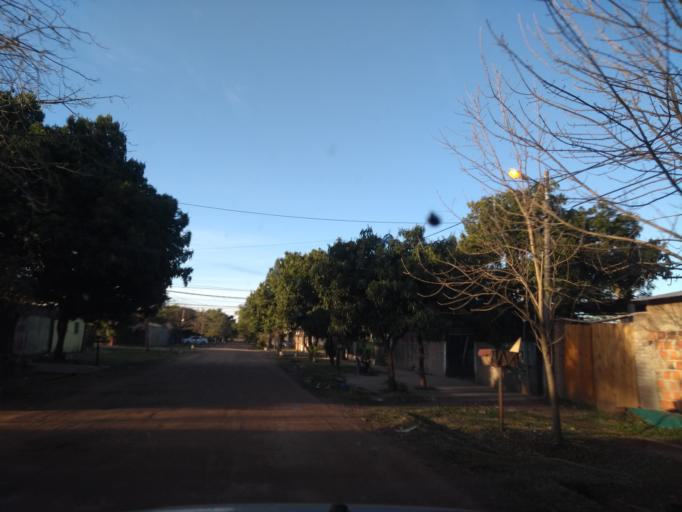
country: AR
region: Chaco
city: Resistencia
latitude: -27.4819
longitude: -58.9654
